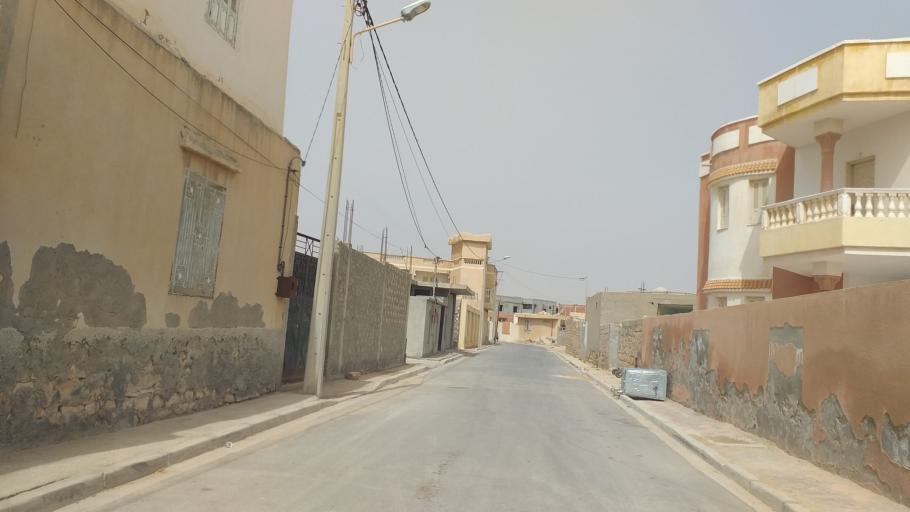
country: TN
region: Qabis
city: Gabes
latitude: 33.9412
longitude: 10.0586
